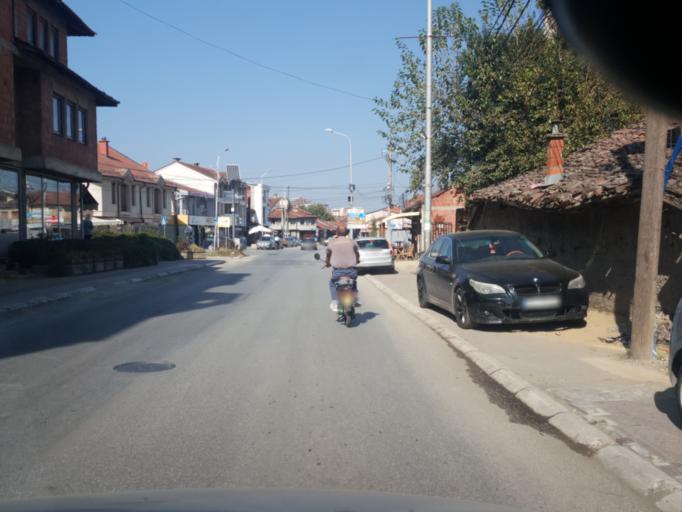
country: XK
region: Gjakova
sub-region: Komuna e Gjakoves
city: Gjakove
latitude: 42.3746
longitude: 20.4251
